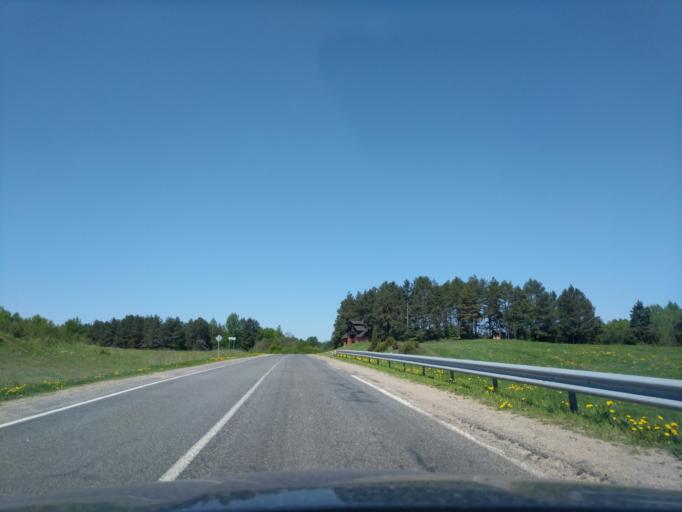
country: BY
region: Minsk
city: Myadzyel
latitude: 54.8948
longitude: 26.9079
